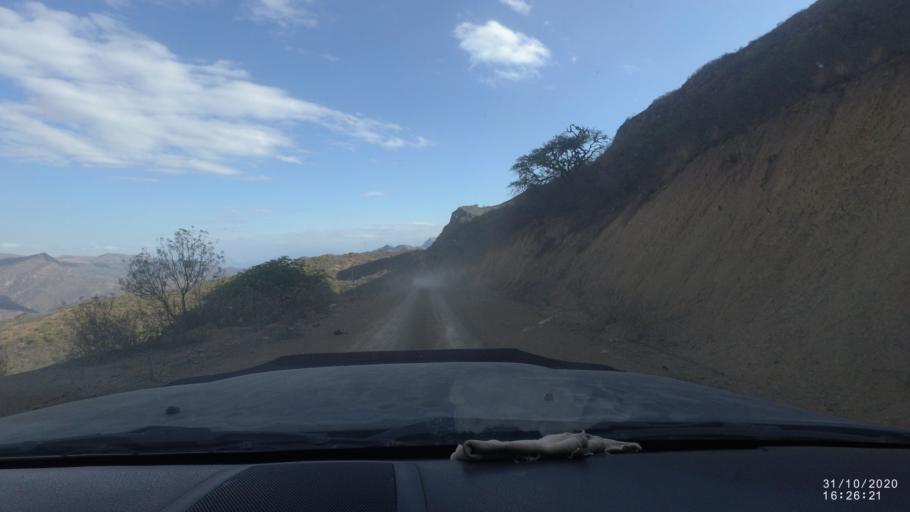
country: BO
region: Chuquisaca
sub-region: Provincia Zudanez
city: Mojocoya
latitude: -18.3973
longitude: -64.5866
